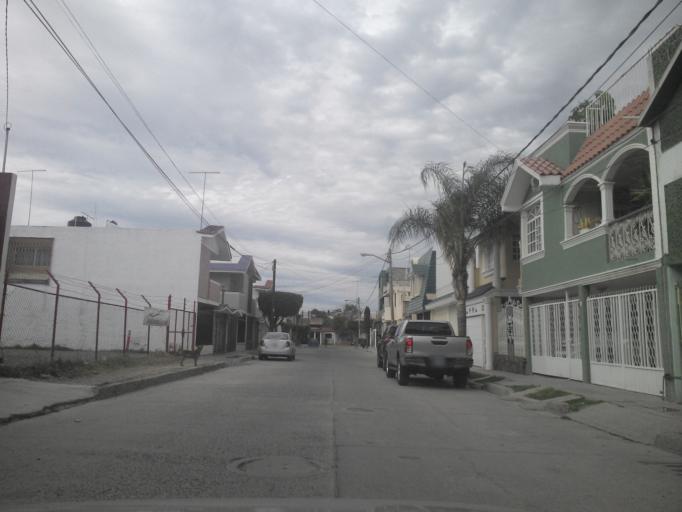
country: MX
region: Guanajuato
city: San Francisco del Rincon
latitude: 21.0106
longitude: -101.8566
